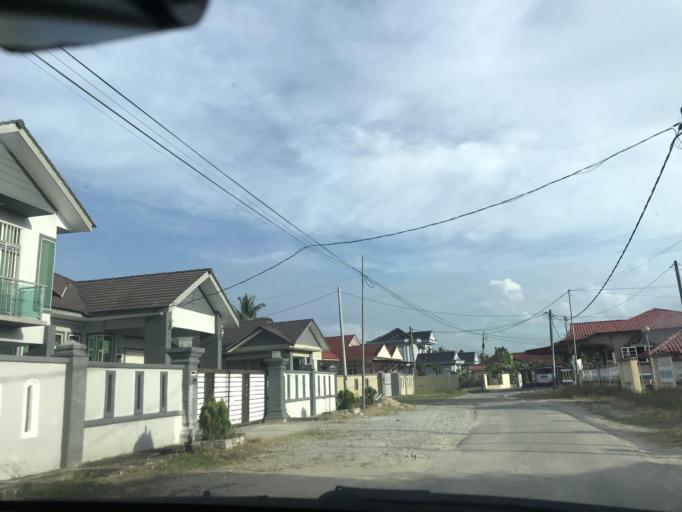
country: MY
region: Kelantan
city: Kota Bharu
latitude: 6.1264
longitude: 102.2231
